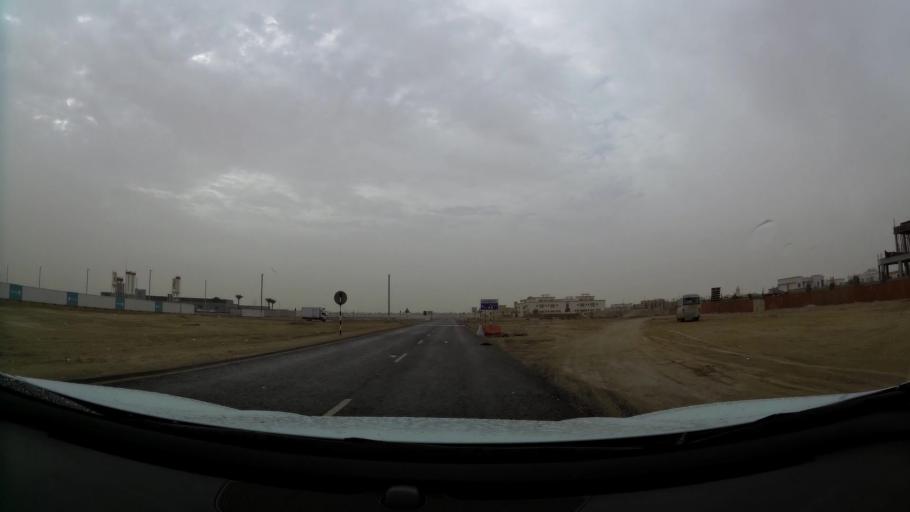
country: AE
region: Abu Dhabi
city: Abu Dhabi
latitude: 24.4183
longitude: 54.6090
